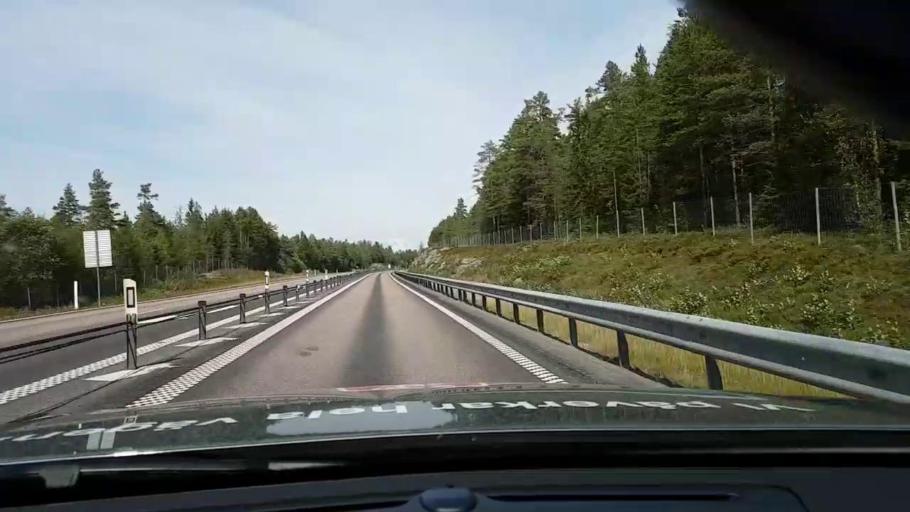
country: SE
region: Vaesternorrland
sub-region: OErnskoeldsviks Kommun
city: Husum
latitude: 63.3769
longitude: 19.1906
